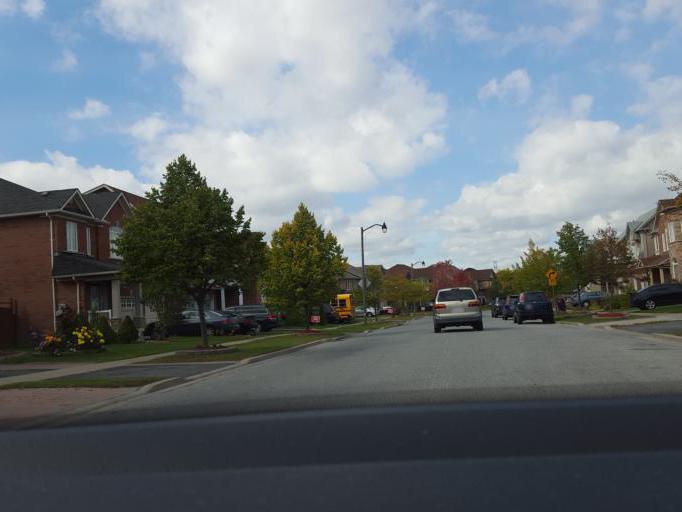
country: CA
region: Ontario
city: Scarborough
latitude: 43.8237
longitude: -79.2191
